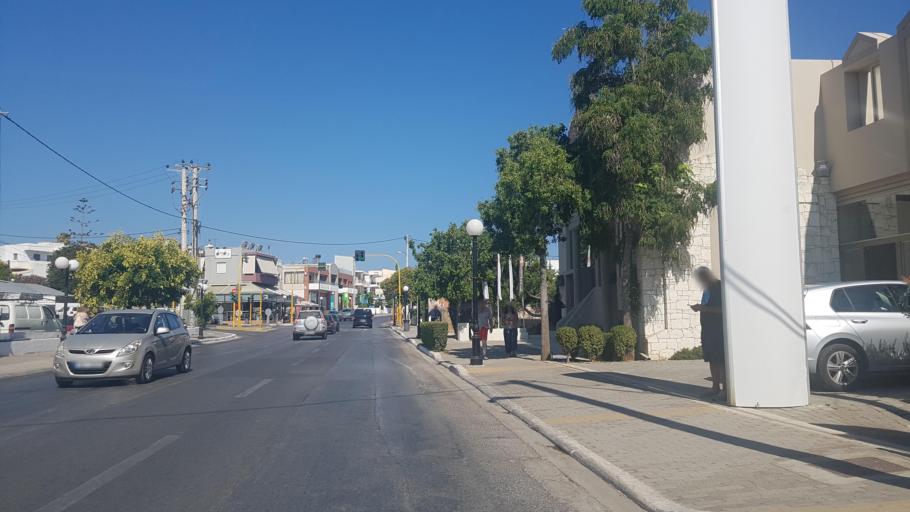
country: GR
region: Crete
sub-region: Nomos Chanias
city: Daratsos
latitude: 35.5076
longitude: 23.9804
